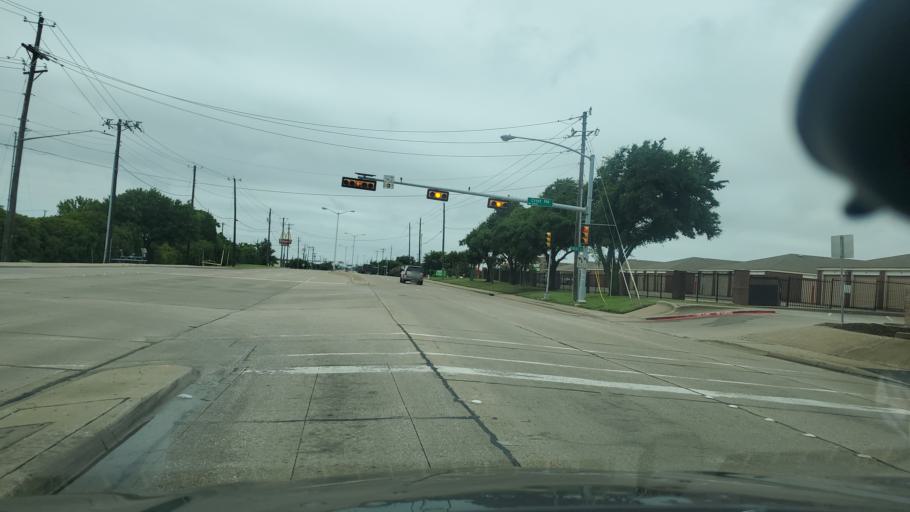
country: US
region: Texas
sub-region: Dallas County
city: Garland
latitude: 32.9337
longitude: -96.6307
